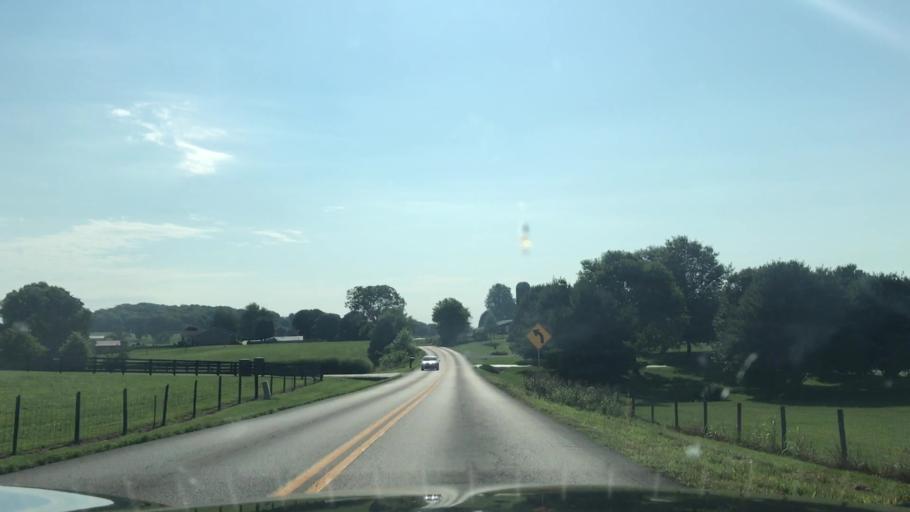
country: US
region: Kentucky
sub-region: Hart County
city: Horse Cave
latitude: 37.1664
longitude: -85.8335
